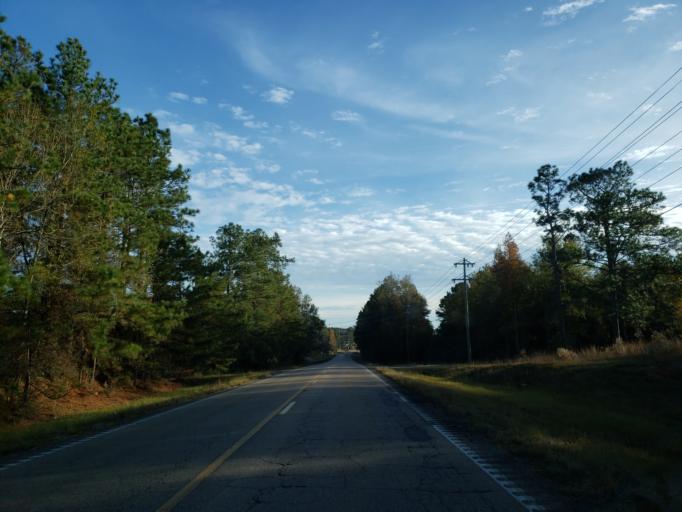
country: US
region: Mississippi
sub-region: Lamar County
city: West Hattiesburg
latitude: 31.3034
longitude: -89.4700
